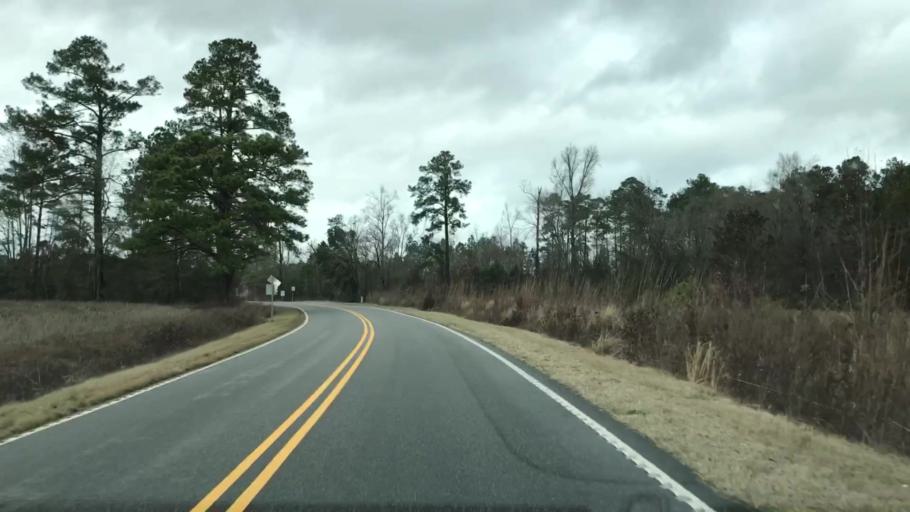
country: US
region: South Carolina
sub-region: Florence County
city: Johnsonville
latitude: 33.6604
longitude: -79.3046
